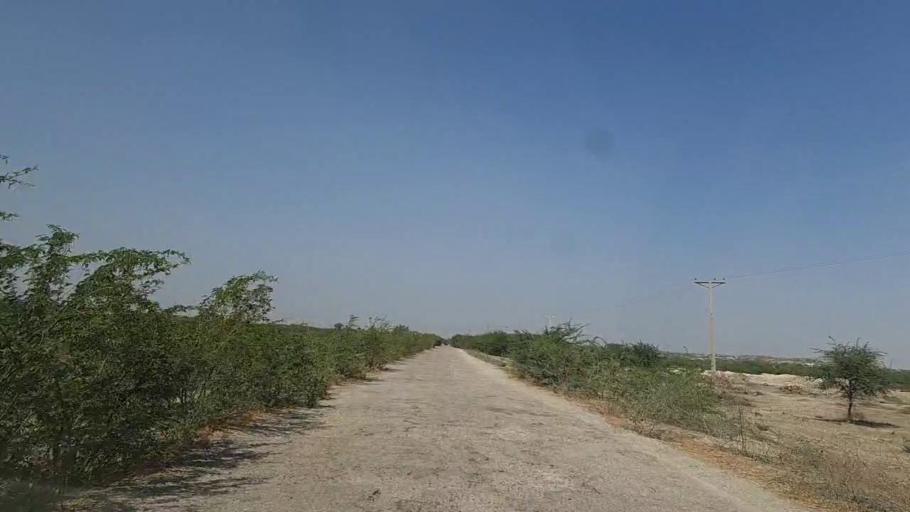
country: PK
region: Sindh
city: Naukot
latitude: 24.6458
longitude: 69.2879
